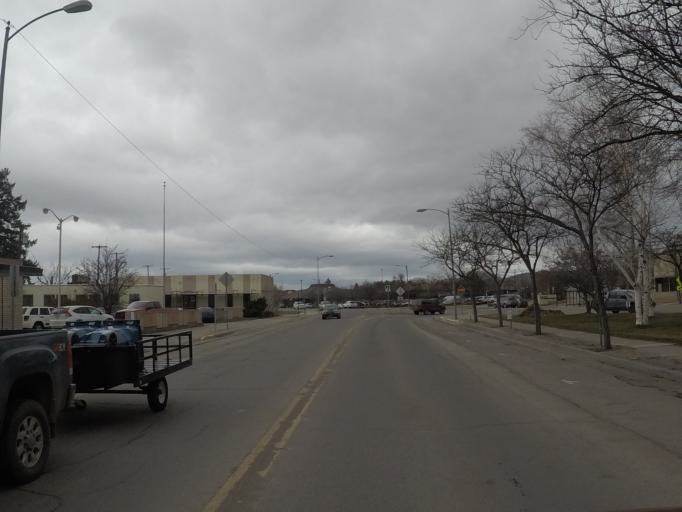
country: US
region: Montana
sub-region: Missoula County
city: Missoula
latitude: 46.8737
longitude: -114.0008
